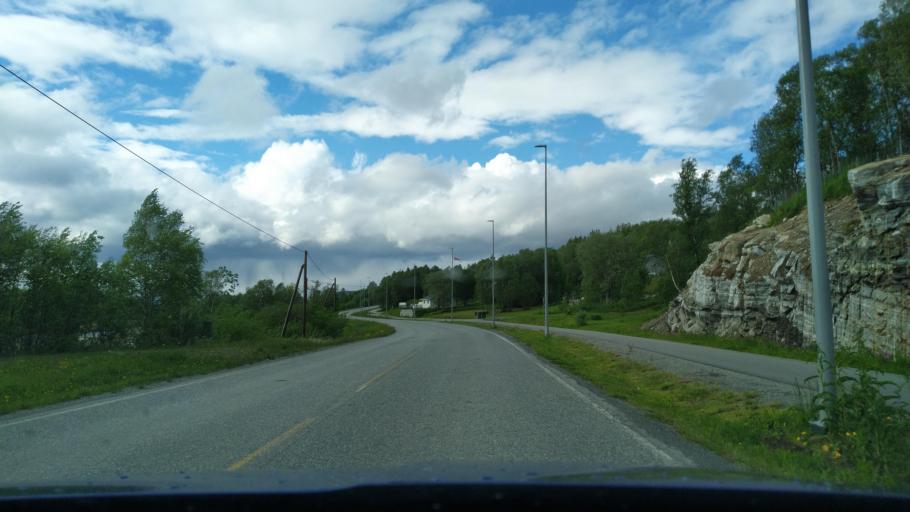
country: NO
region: Troms
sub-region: Lenvik
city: Finnsnes
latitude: 69.1803
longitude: 18.0576
